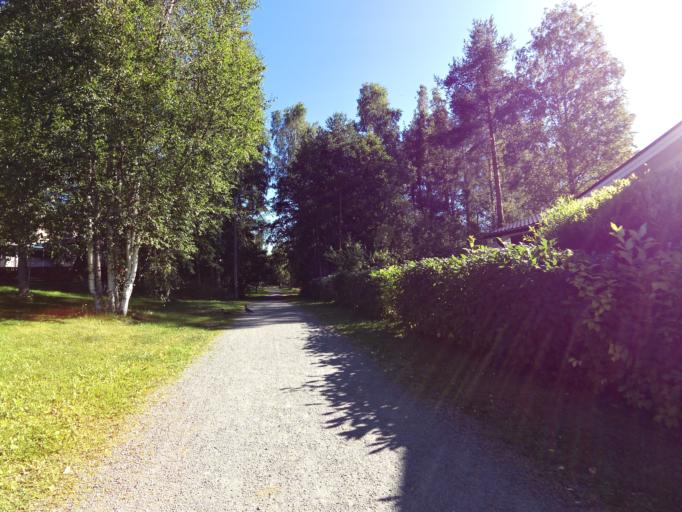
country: FI
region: Pirkanmaa
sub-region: Tampere
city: Yloejaervi
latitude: 61.5085
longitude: 23.6036
